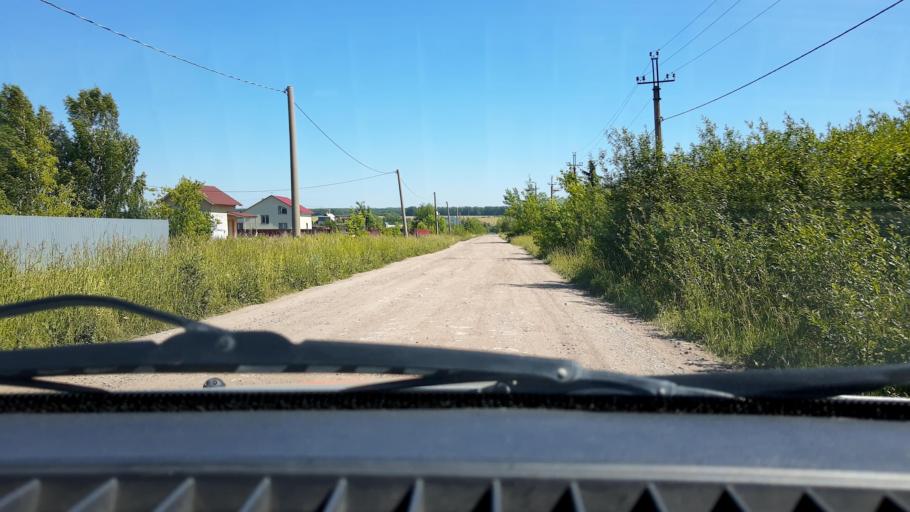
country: RU
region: Bashkortostan
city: Avdon
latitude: 54.5464
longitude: 55.7185
